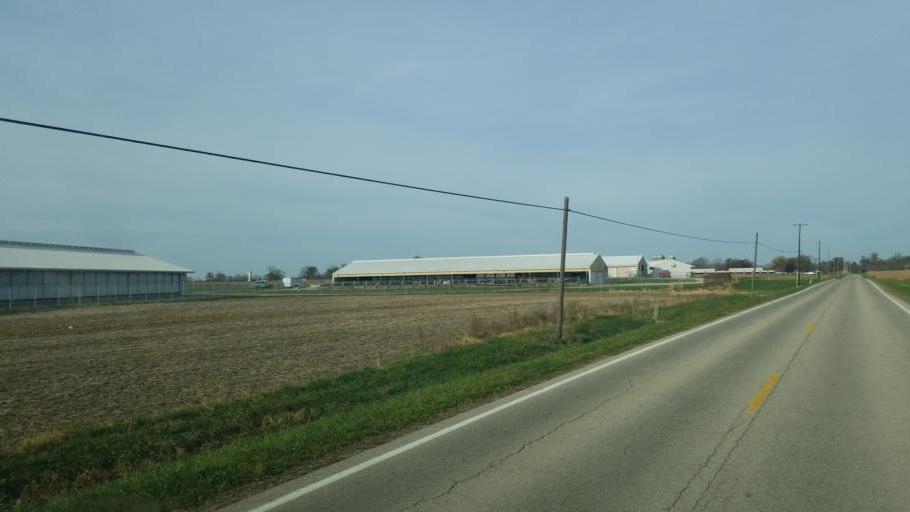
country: US
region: Ohio
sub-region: Madison County
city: Plain City
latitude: 40.1338
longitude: -83.3261
